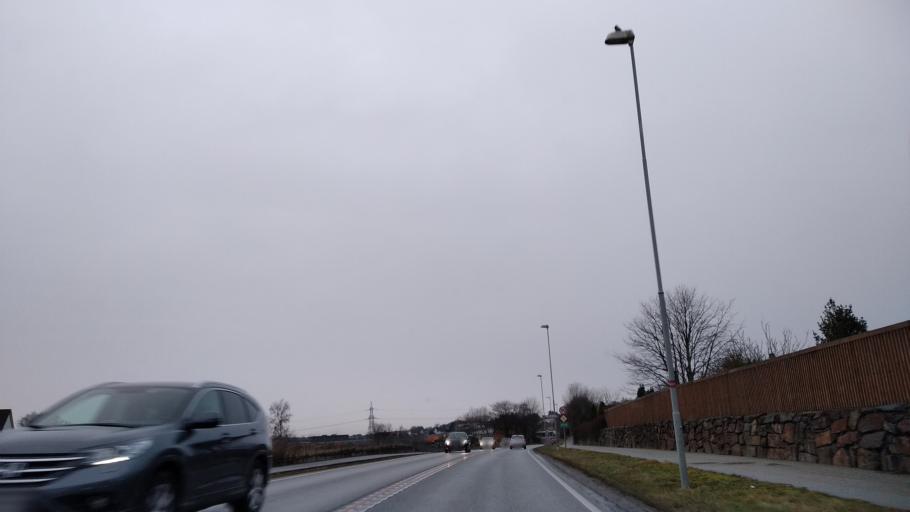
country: NO
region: Rogaland
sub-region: Sola
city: Sola
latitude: 58.9519
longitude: 5.6631
